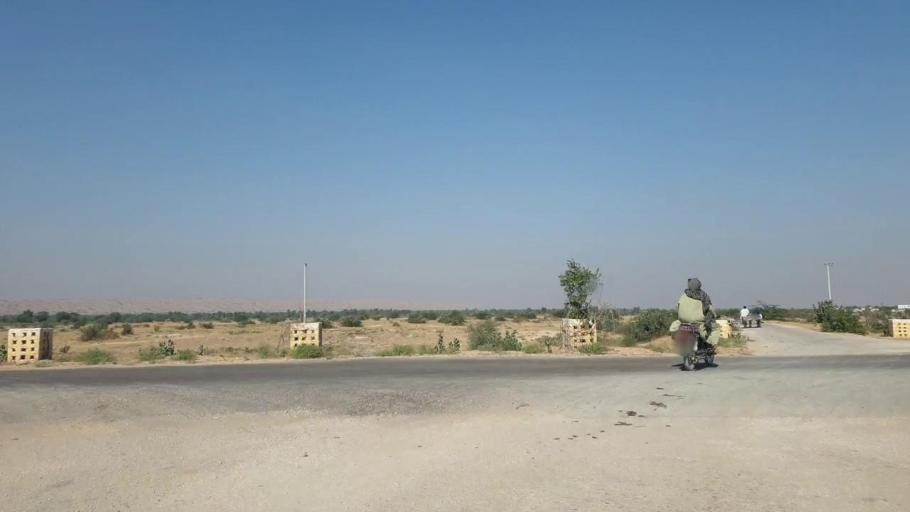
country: PK
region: Sindh
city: Jamshoro
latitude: 25.3700
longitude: 67.8407
